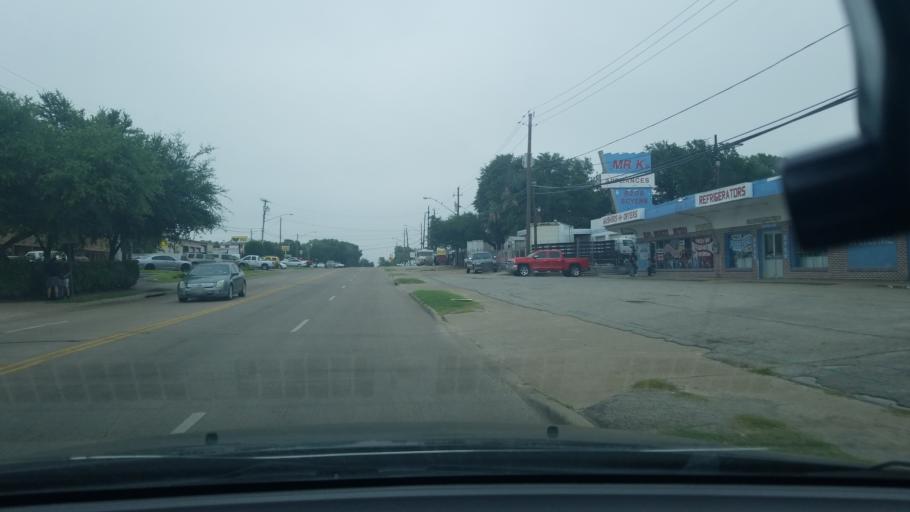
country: US
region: Texas
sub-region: Dallas County
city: Balch Springs
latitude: 32.7633
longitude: -96.6800
